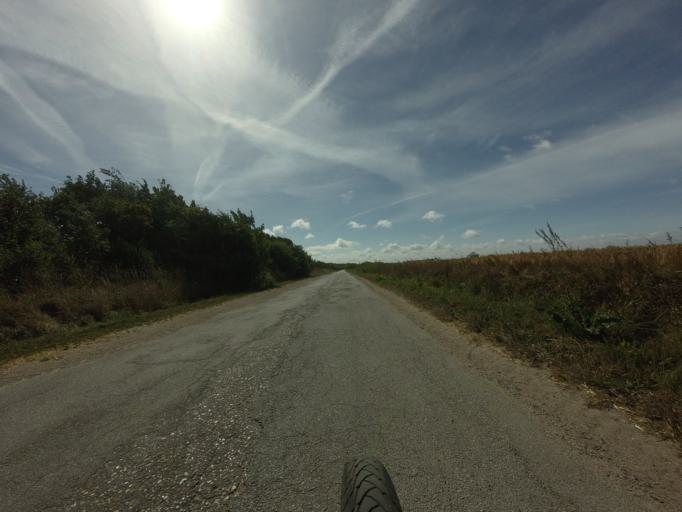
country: DK
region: North Denmark
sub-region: Hjorring Kommune
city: Vra
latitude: 57.3387
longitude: 9.8092
